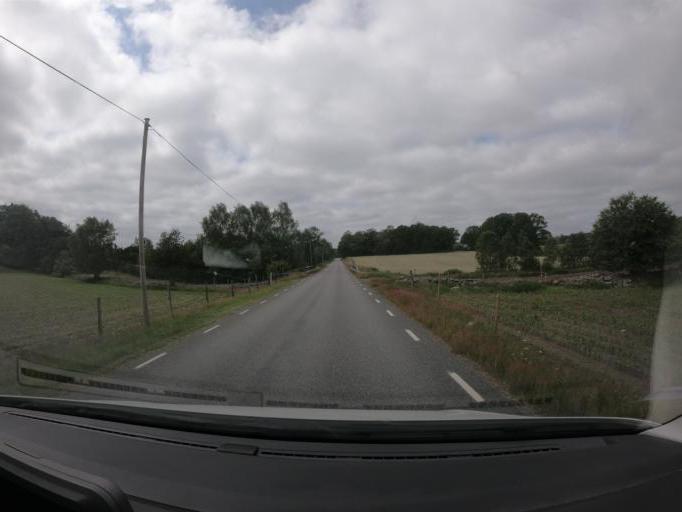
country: SE
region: Skane
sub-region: Hassleholms Kommun
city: Sosdala
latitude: 56.0644
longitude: 13.5523
